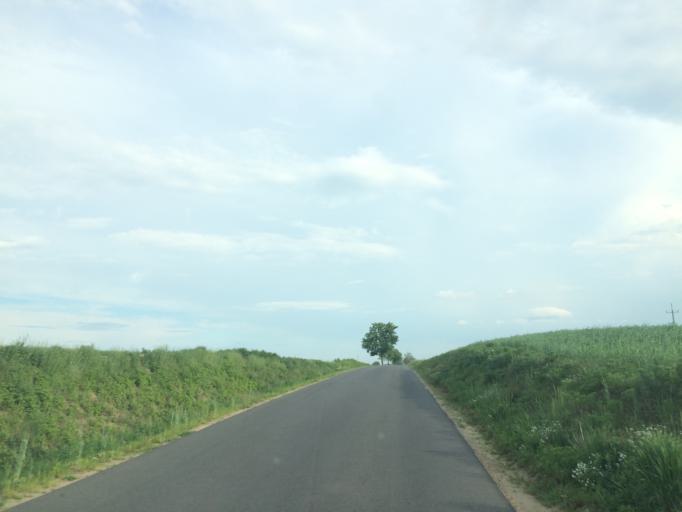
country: PL
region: Kujawsko-Pomorskie
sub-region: Powiat brodnicki
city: Brzozie
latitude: 53.3815
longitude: 19.7070
